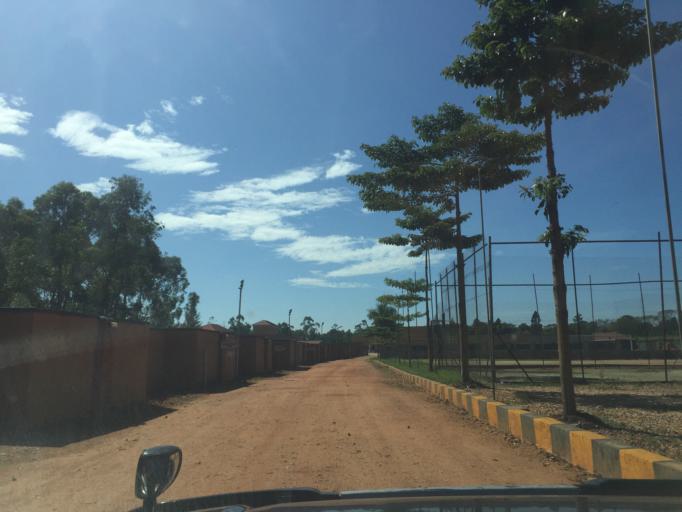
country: UG
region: Central Region
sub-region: Luwero District
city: Luwero
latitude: 0.8456
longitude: 32.5107
